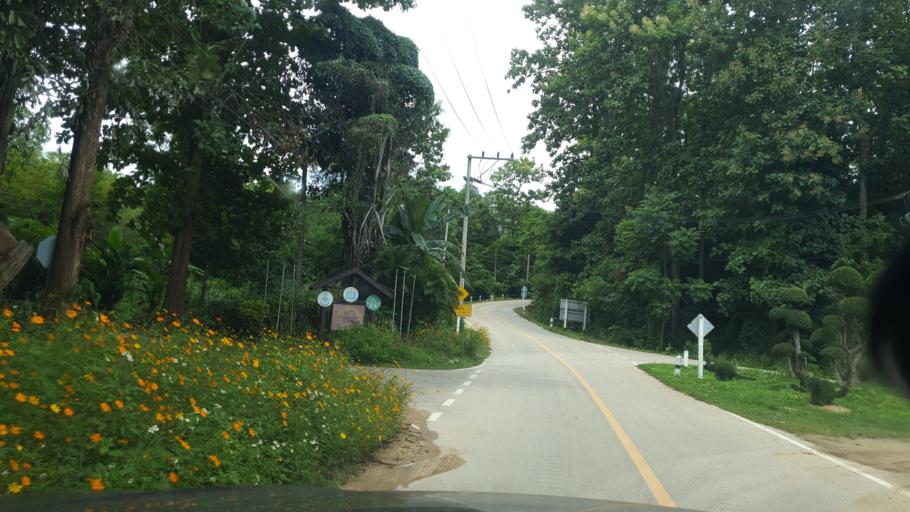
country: TH
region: Lampang
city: Hang Chat
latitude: 18.3606
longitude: 99.2583
